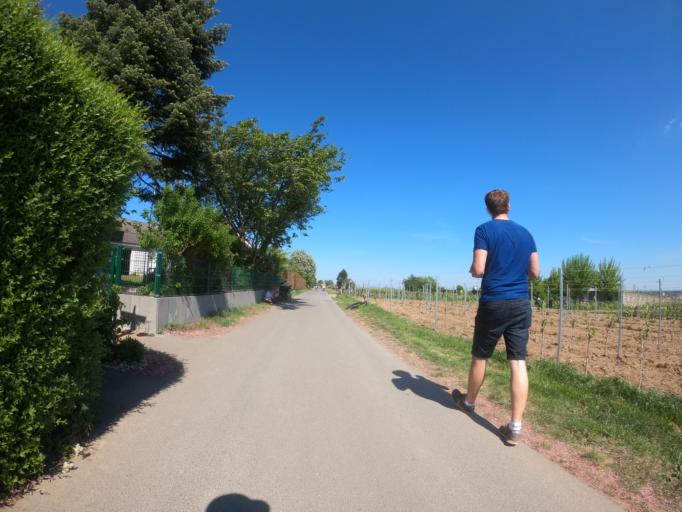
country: DE
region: Hesse
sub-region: Regierungsbezirk Darmstadt
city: Florsheim
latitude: 50.0238
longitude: 8.4096
